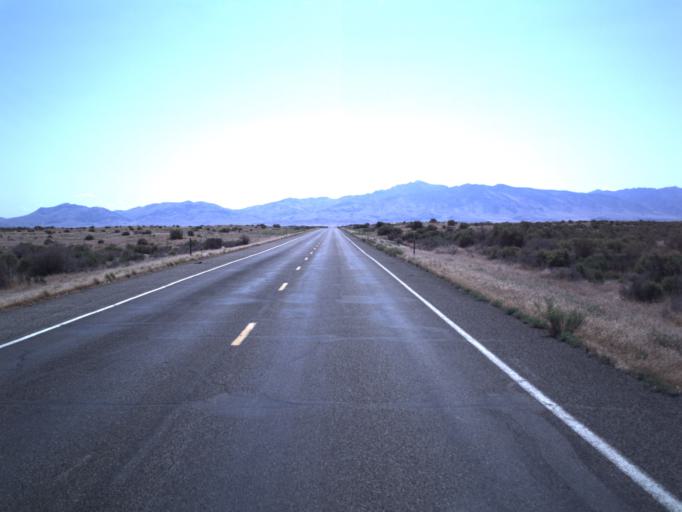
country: US
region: Utah
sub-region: Millard County
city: Delta
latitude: 39.4819
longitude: -112.5165
